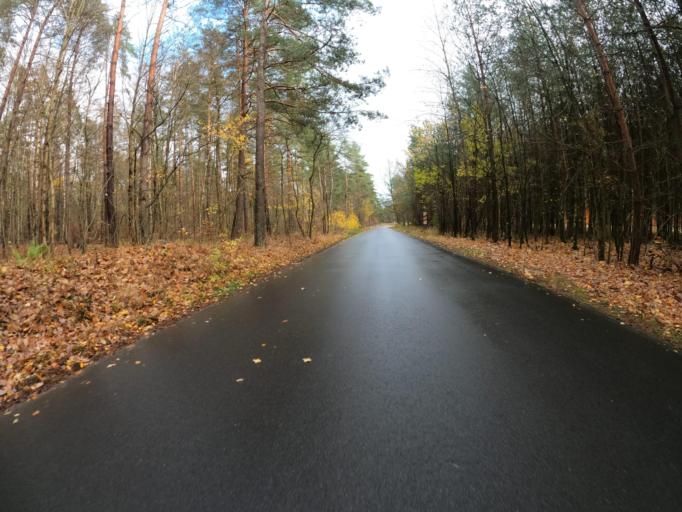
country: PL
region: West Pomeranian Voivodeship
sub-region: Powiat walecki
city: Tuczno
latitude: 53.2321
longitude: 16.2606
